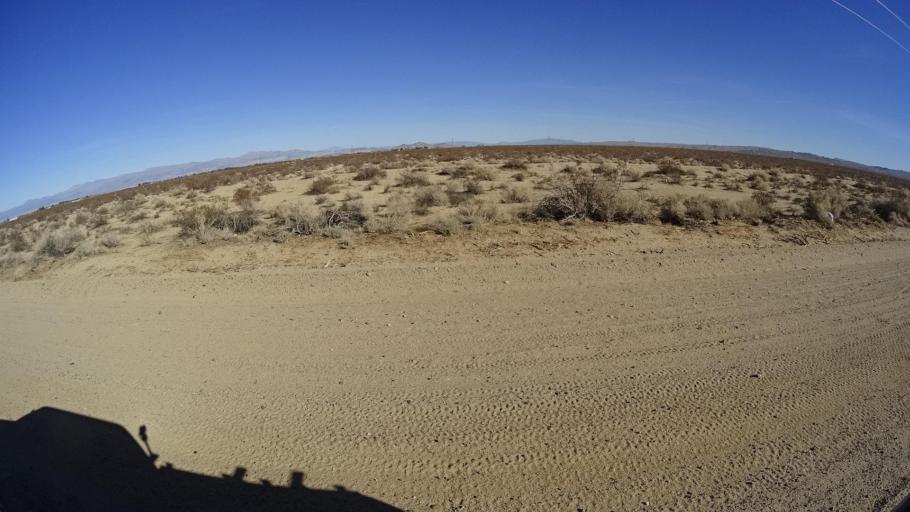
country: US
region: California
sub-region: Kern County
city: Inyokern
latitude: 35.6139
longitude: -117.8025
